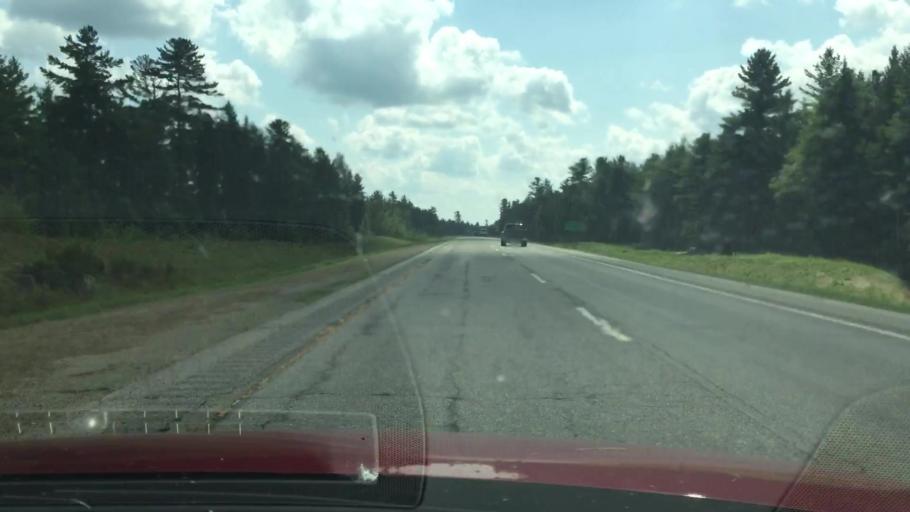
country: US
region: Maine
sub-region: Penobscot County
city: Medway
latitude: 45.5803
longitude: -68.5436
